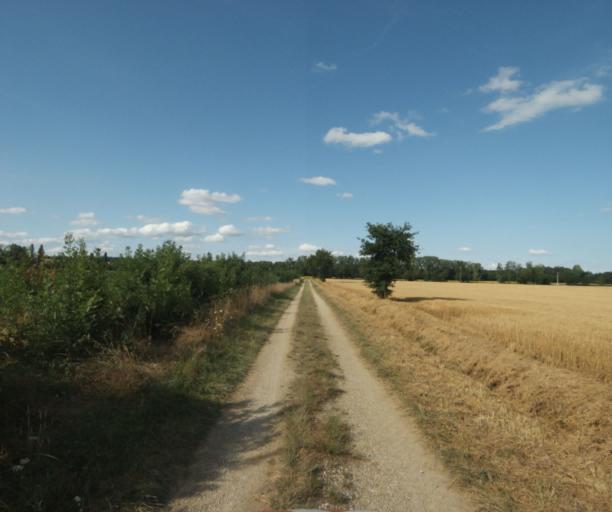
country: FR
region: Midi-Pyrenees
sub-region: Departement du Tarn
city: Puylaurens
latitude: 43.5194
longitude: 2.0006
